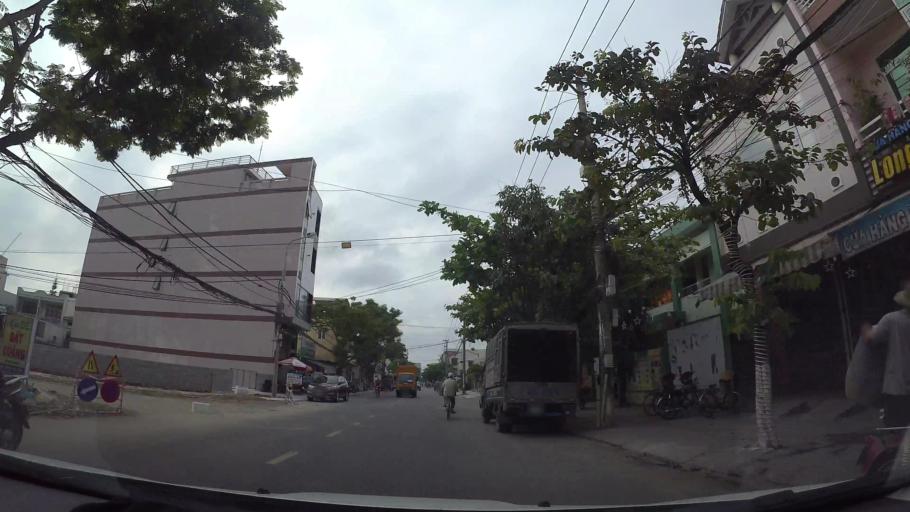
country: VN
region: Da Nang
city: Son Tra
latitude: 16.0652
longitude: 108.2409
